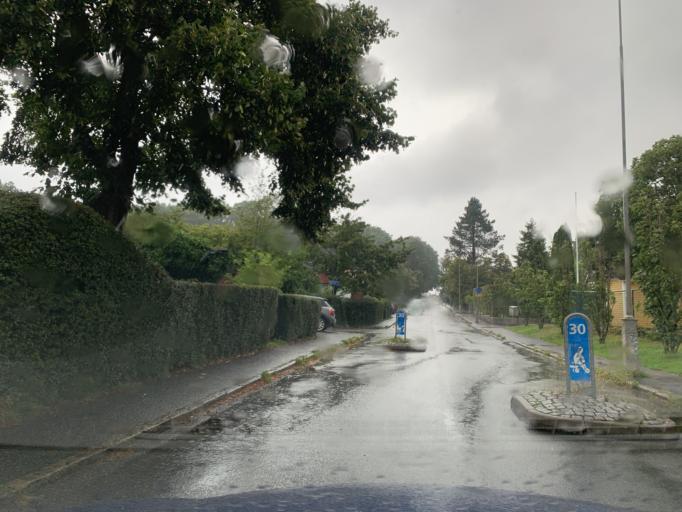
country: SE
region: Vaestra Goetaland
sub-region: Goteborg
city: Goeteborg
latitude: 57.7054
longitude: 12.0146
